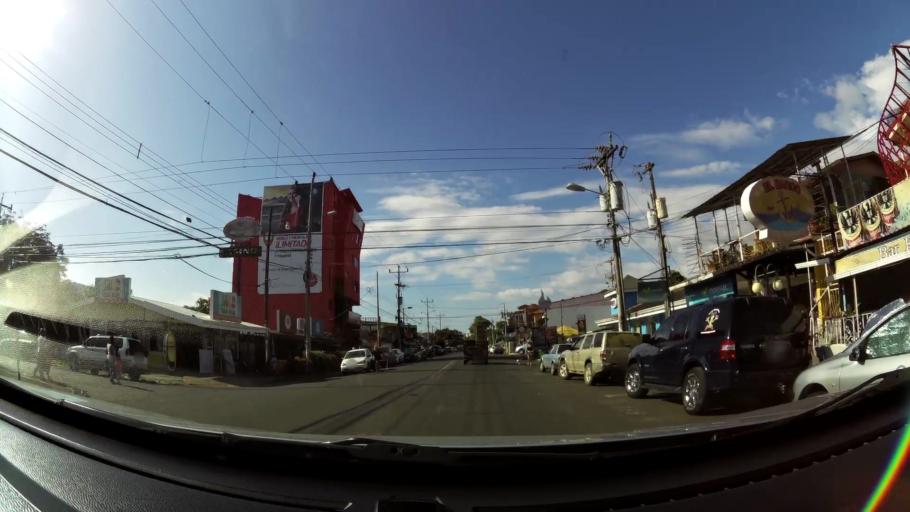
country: CR
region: Puntarenas
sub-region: Canton de Garabito
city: Jaco
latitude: 9.6138
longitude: -84.6275
